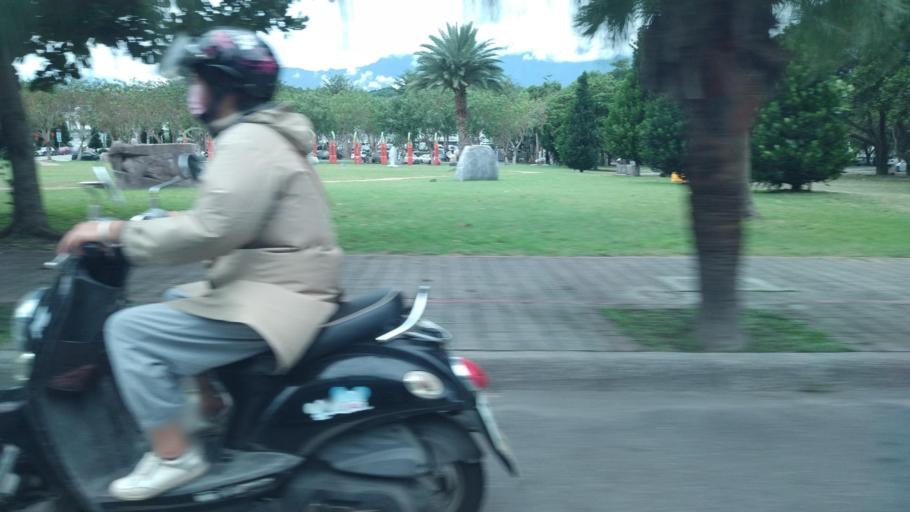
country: TW
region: Taiwan
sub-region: Hualien
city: Hualian
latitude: 23.9918
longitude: 121.6218
